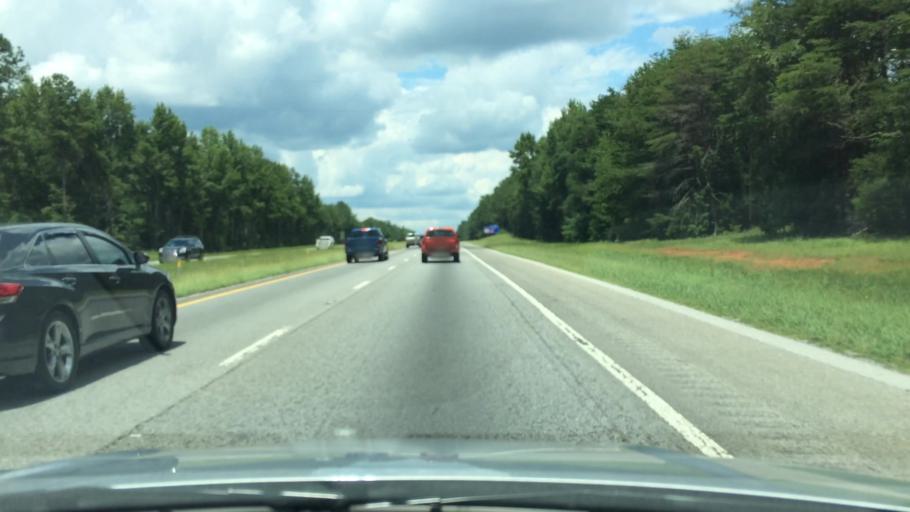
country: US
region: South Carolina
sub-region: Spartanburg County
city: Woodruff
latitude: 34.6878
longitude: -81.9392
